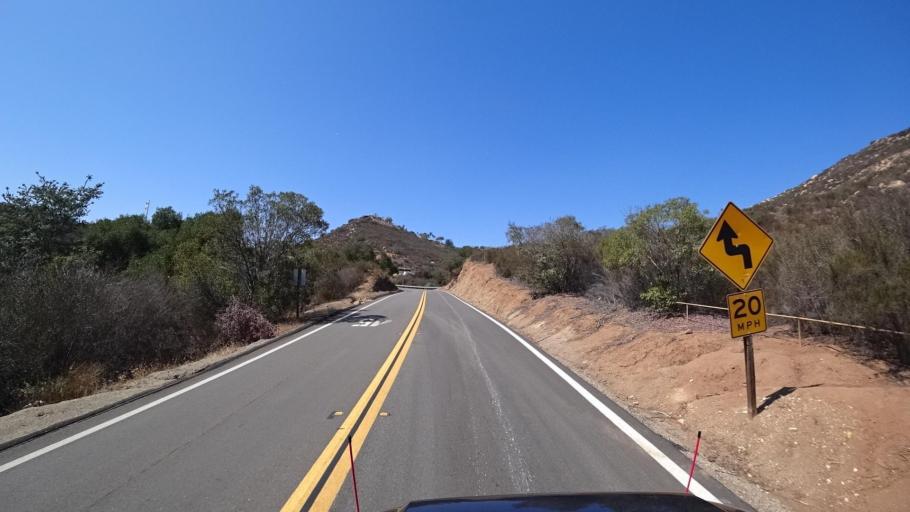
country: US
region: California
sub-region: San Diego County
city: Harbison Canyon
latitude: 32.8271
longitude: -116.8354
